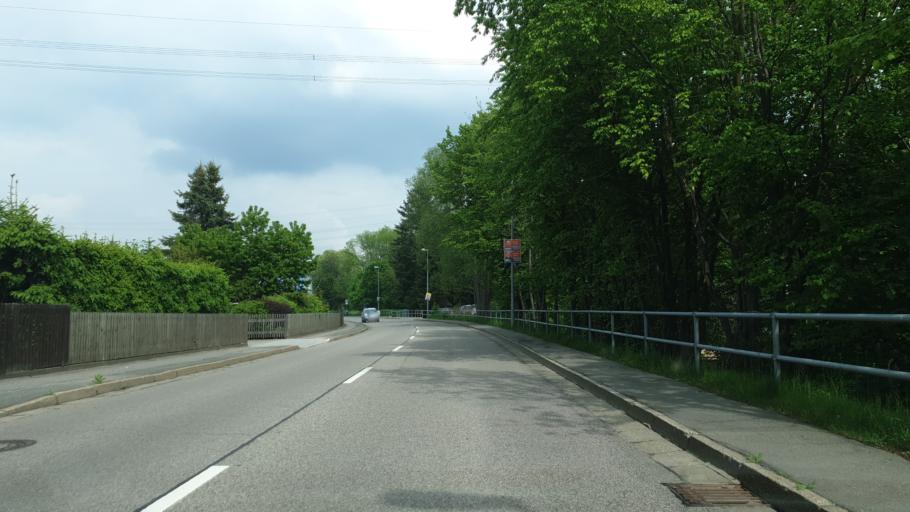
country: DE
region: Saxony
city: Hartmannsdorf
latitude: 50.8619
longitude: 12.8104
